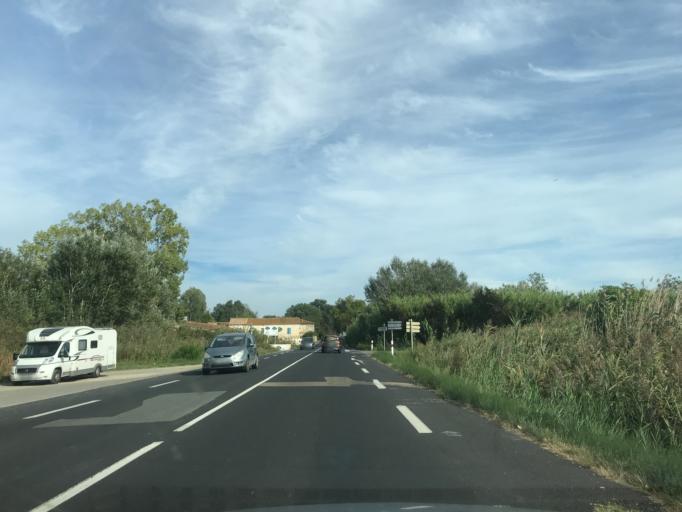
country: FR
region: Provence-Alpes-Cote d'Azur
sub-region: Departement des Bouches-du-Rhone
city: Saintes-Maries-de-la-Mer
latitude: 43.5483
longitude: 4.3450
